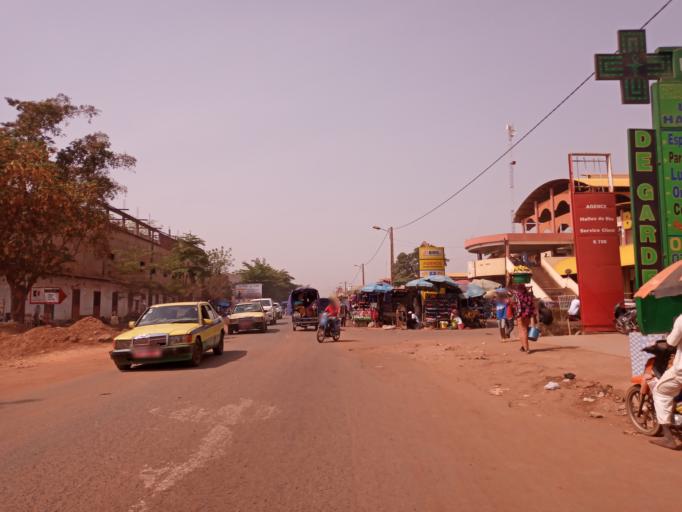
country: ML
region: Bamako
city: Bamako
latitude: 12.5951
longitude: -7.9615
